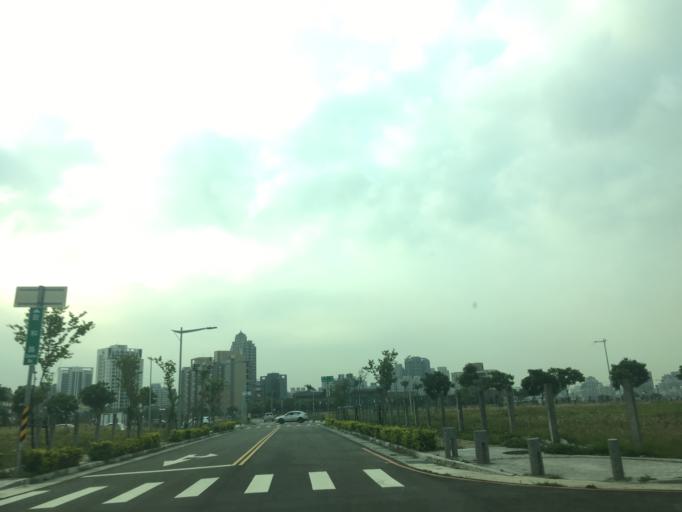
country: TW
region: Taiwan
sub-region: Taichung City
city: Taichung
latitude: 24.1902
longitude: 120.6776
